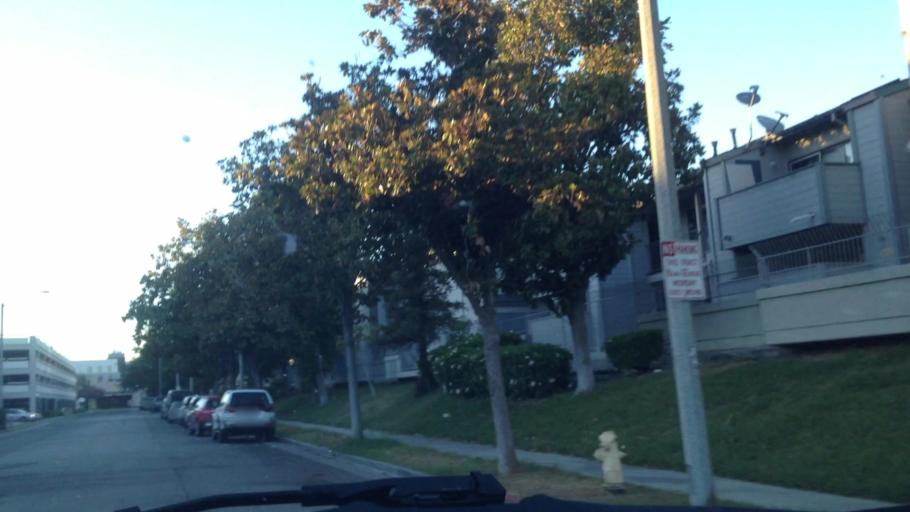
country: US
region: California
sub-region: Orange County
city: Anaheim
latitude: 33.8302
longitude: -117.9170
